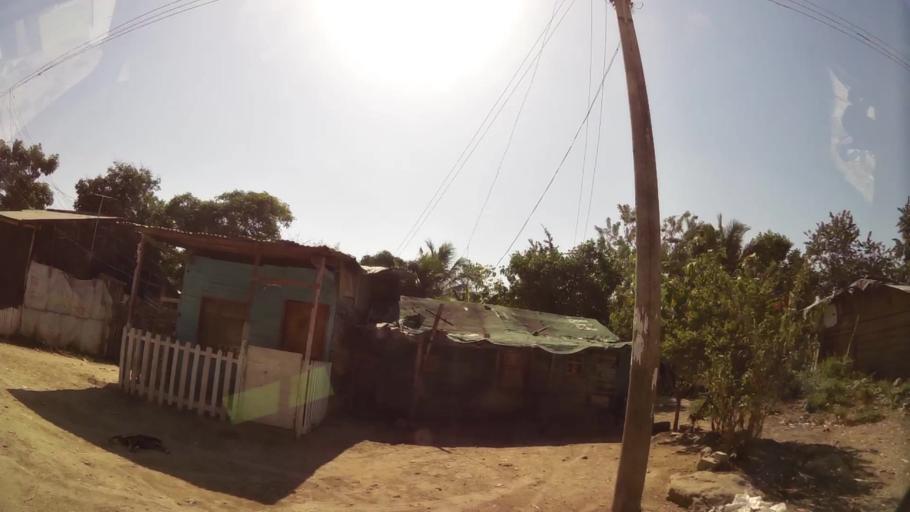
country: CO
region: Bolivar
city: Cartagena
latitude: 10.3679
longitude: -75.4934
